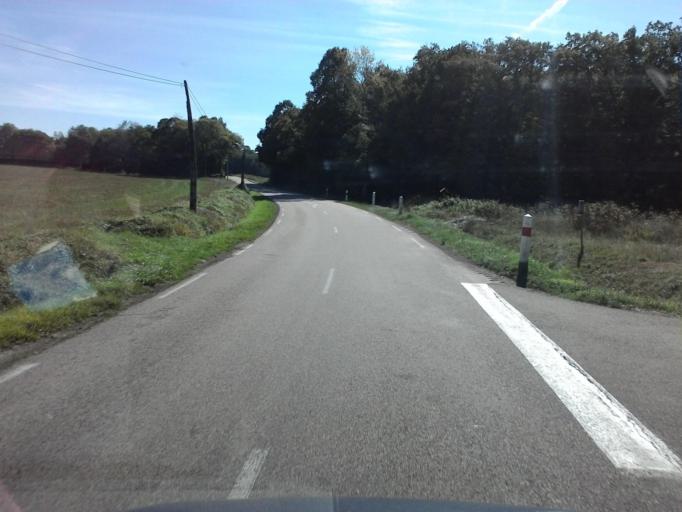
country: FR
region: Bourgogne
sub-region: Departement de l'Yonne
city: Joux-la-Ville
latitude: 47.5951
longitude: 3.8645
